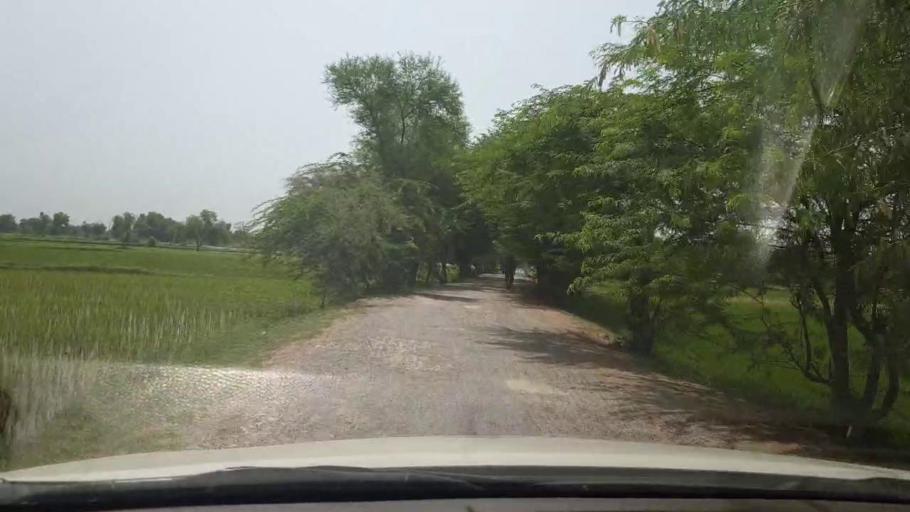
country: PK
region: Sindh
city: Shikarpur
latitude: 28.0206
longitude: 68.6470
